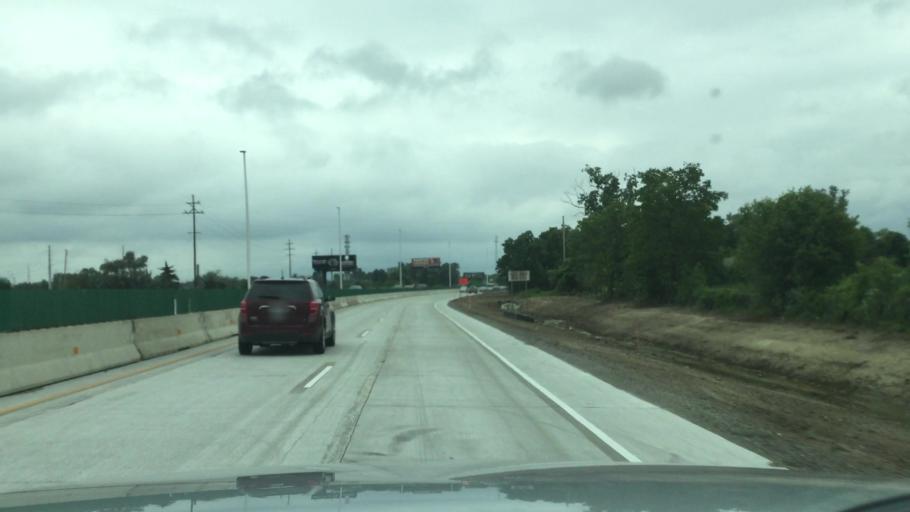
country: US
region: Michigan
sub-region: Genesee County
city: Flint
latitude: 42.9886
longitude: -83.7190
